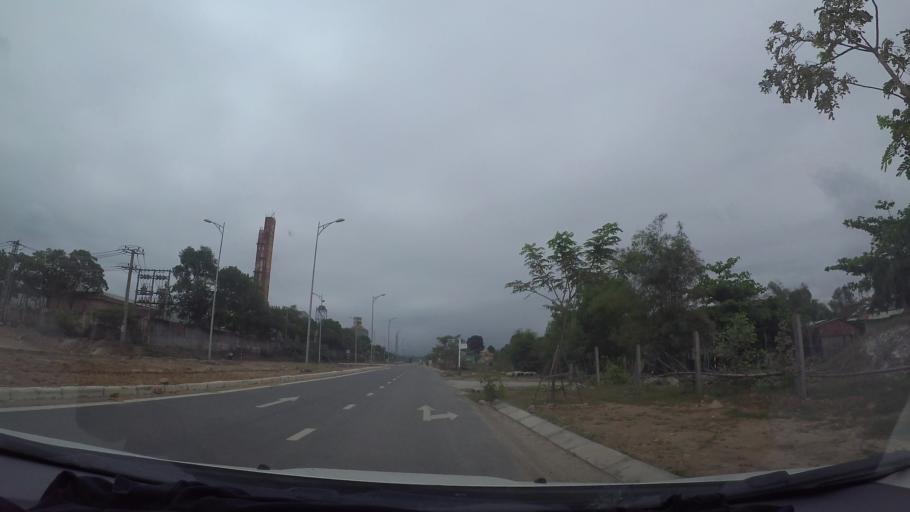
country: VN
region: Da Nang
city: Lien Chieu
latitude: 16.0885
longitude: 108.1057
